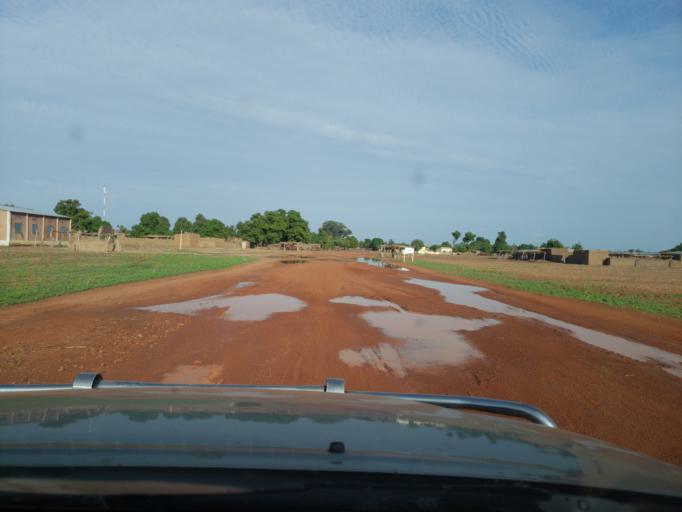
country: ML
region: Sikasso
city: Koutiala
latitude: 12.4229
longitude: -5.6788
